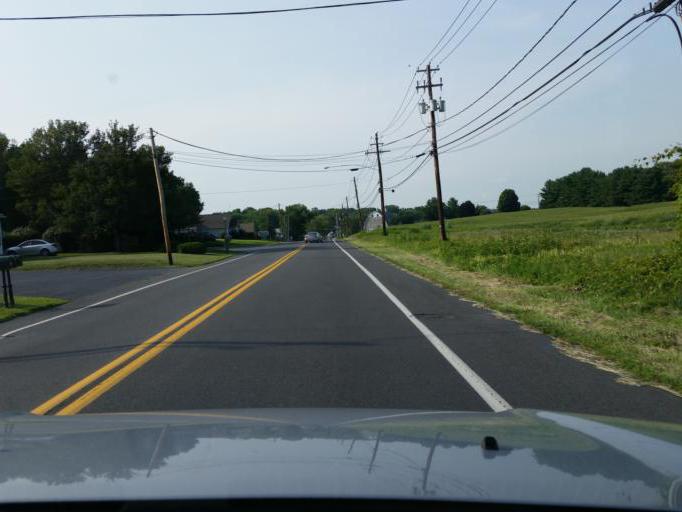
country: US
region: Pennsylvania
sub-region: Dauphin County
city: Hershey
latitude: 40.2711
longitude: -76.6481
